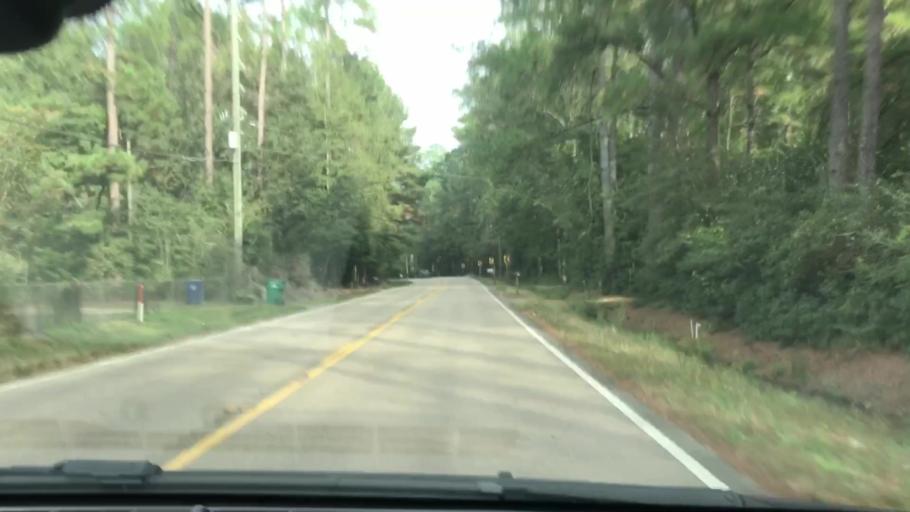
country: US
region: Louisiana
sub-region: Saint Tammany Parish
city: Abita Springs
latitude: 30.4907
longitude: -90.0178
